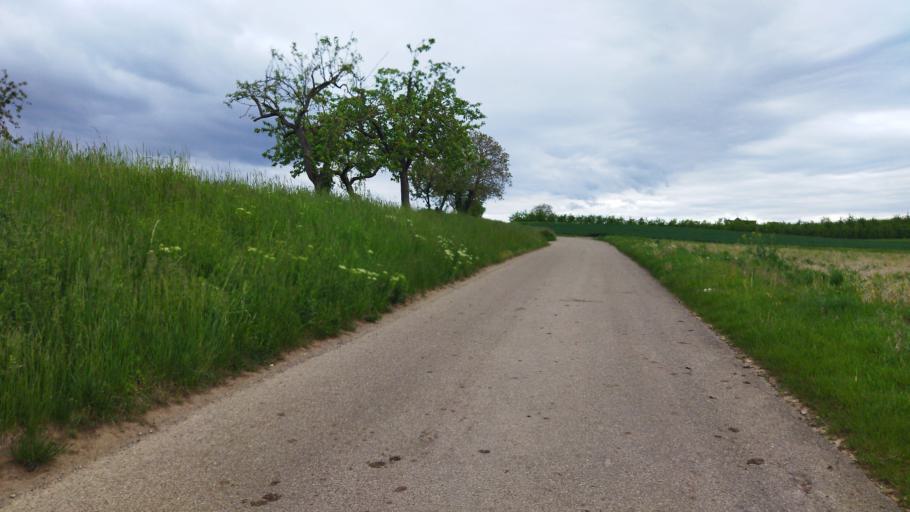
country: DE
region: Baden-Wuerttemberg
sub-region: Regierungsbezirk Stuttgart
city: Lauffen am Neckar
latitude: 49.0862
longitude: 9.1586
